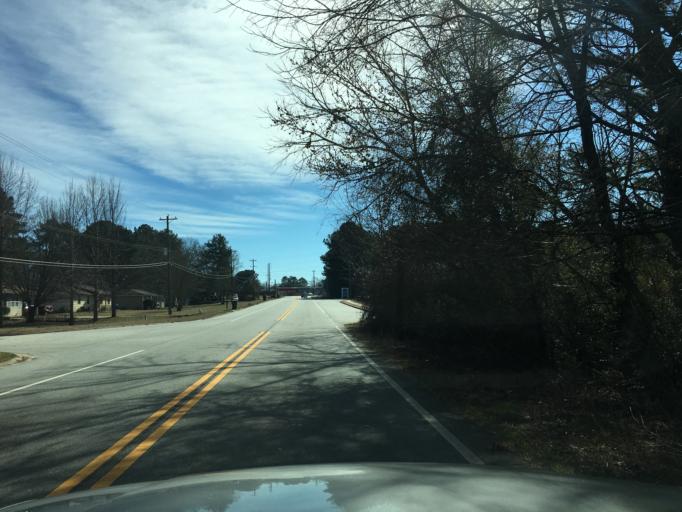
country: US
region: Georgia
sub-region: Rockdale County
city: Lakeview Estates
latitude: 33.6921
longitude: -84.0220
